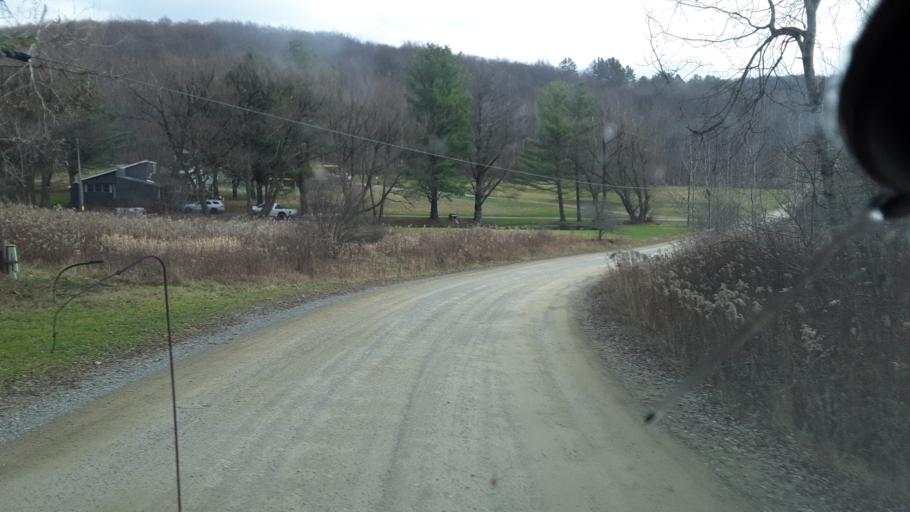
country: US
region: Pennsylvania
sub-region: Tioga County
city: Westfield
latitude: 41.9219
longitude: -77.7191
